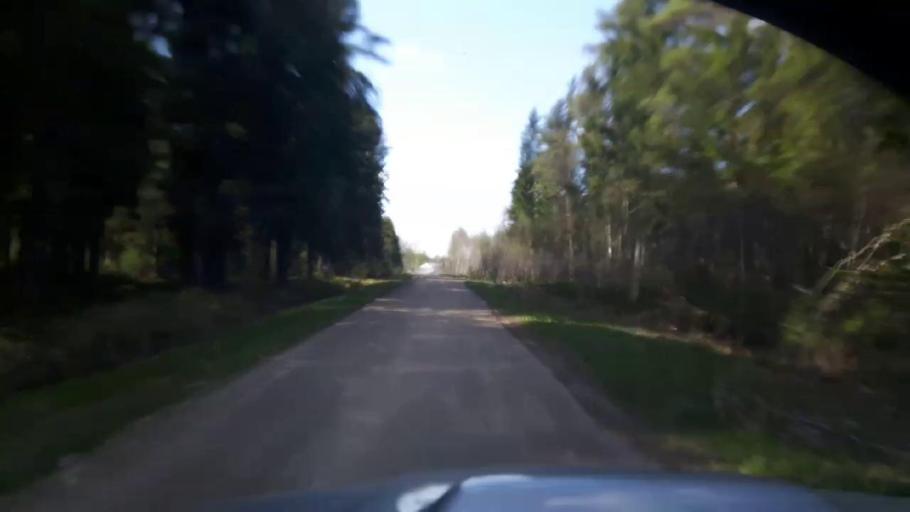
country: EE
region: Paernumaa
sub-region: Tootsi vald
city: Tootsi
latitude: 58.4469
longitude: 24.8670
